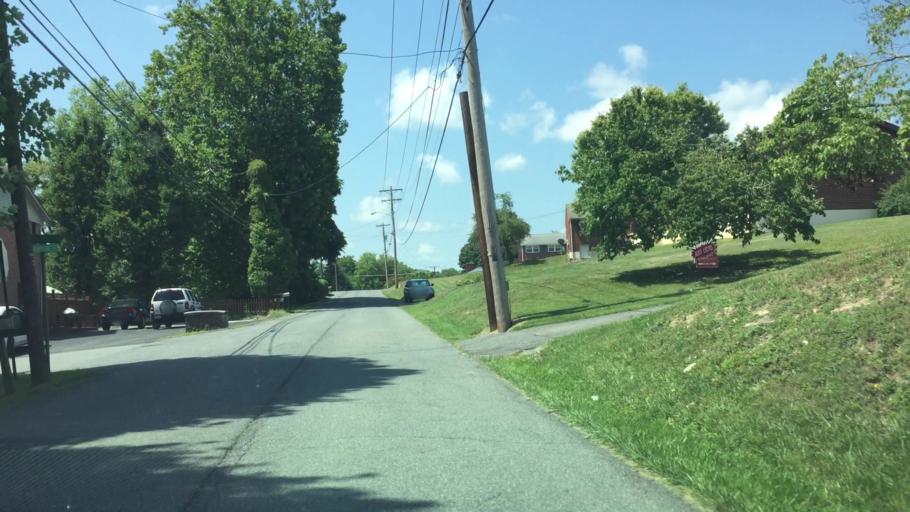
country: US
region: Virginia
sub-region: Pulaski County
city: Pulaski
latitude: 37.0578
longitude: -80.7508
